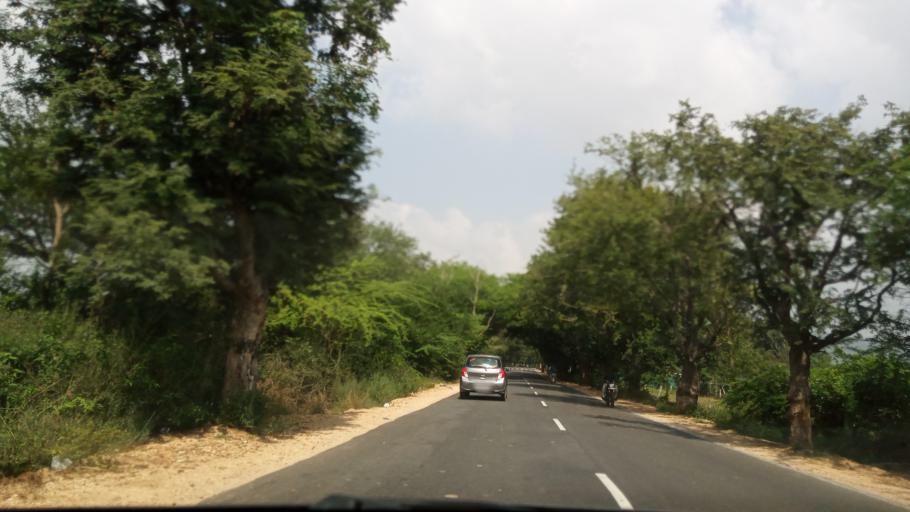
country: IN
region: Andhra Pradesh
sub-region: Chittoor
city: Madanapalle
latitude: 13.6260
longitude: 78.5494
